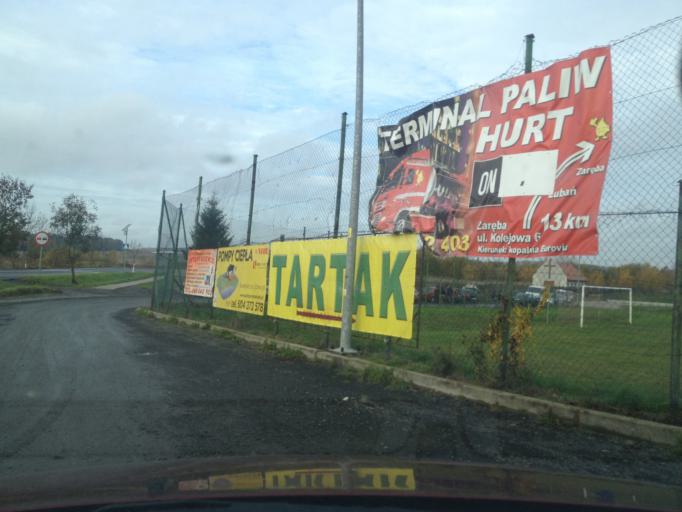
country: PL
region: Lower Silesian Voivodeship
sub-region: Powiat lubanski
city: Pisarzowice
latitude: 51.1380
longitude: 15.2384
